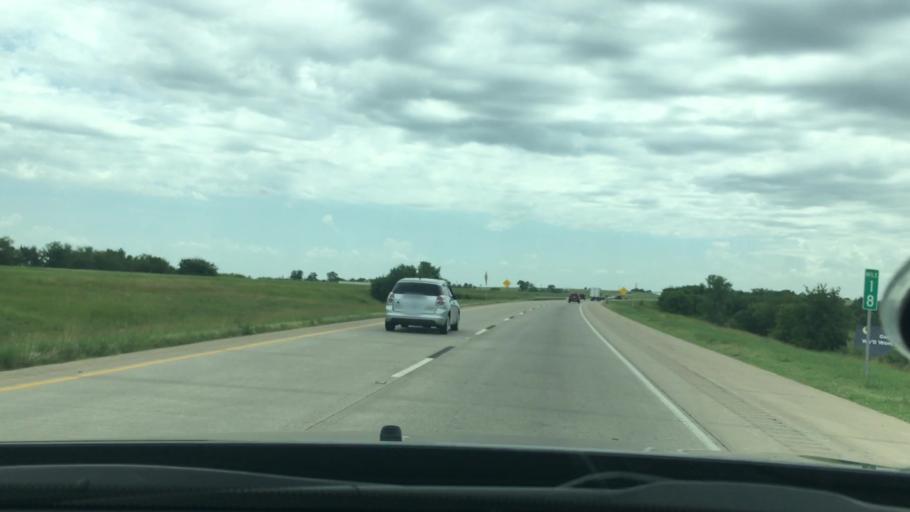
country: US
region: Oklahoma
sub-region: Love County
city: Marietta
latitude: 33.9793
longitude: -97.1352
